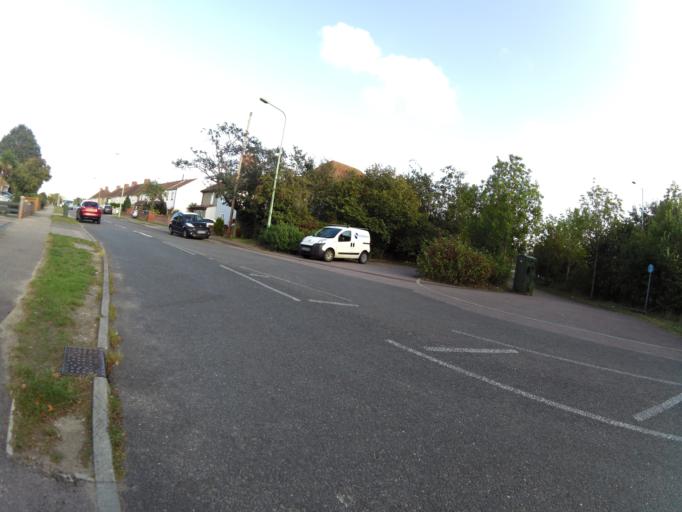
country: GB
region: England
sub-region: Suffolk
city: Kessingland
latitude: 52.4538
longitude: 1.7092
